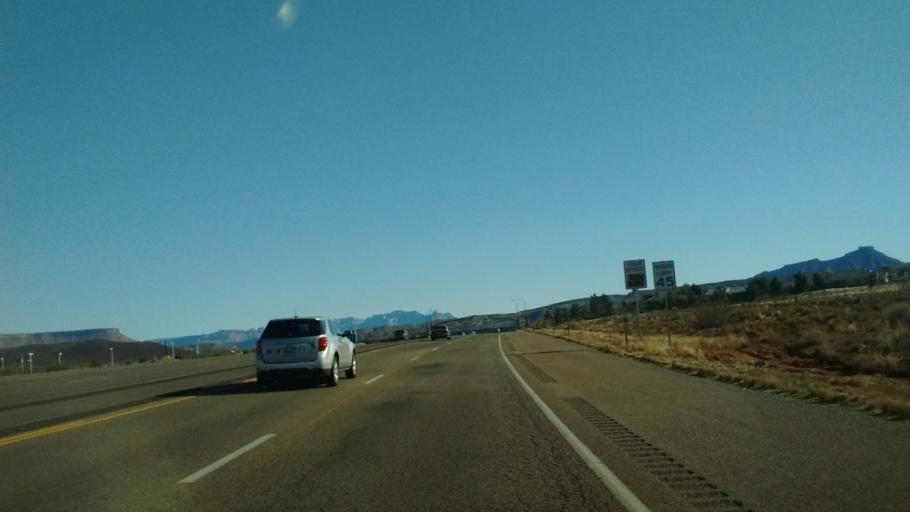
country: US
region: Utah
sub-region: Washington County
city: Hurricane
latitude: 37.1763
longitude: -113.3332
